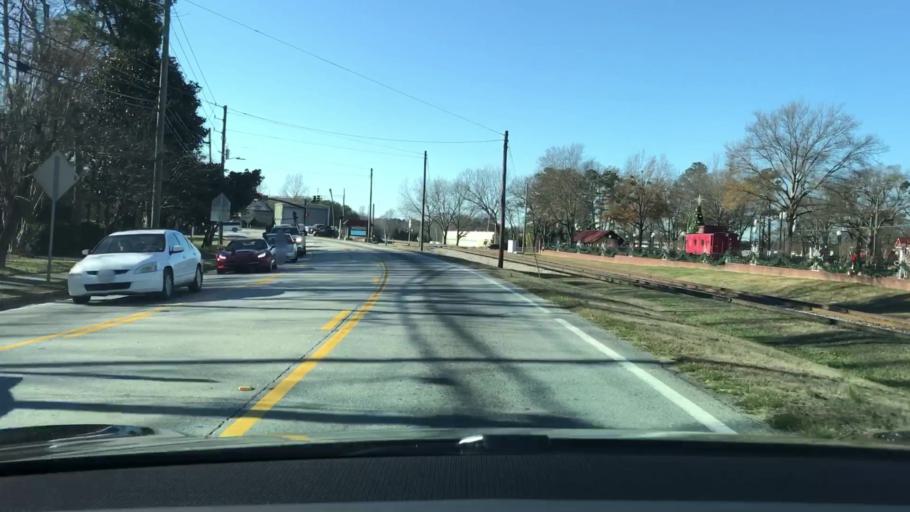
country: US
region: Georgia
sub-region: Barrow County
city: Auburn
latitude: 34.0127
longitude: -83.8267
